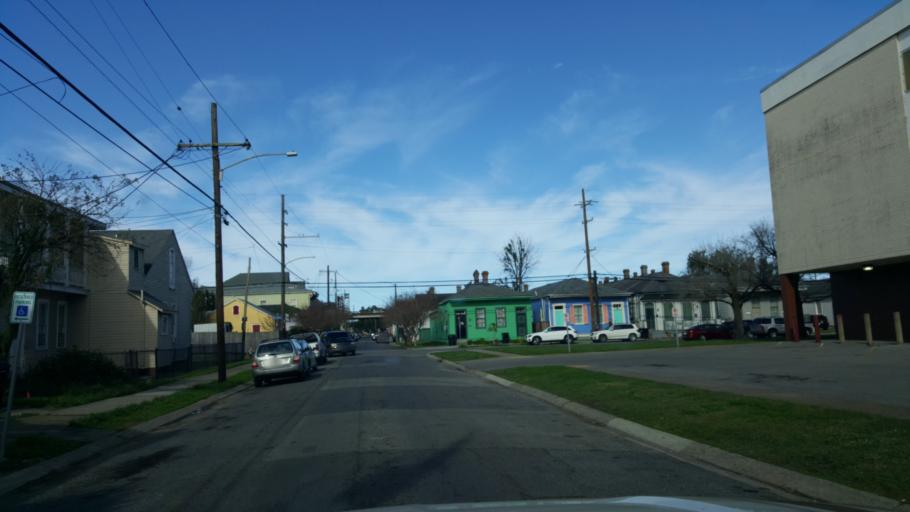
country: US
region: Louisiana
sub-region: Orleans Parish
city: New Orleans
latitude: 29.9687
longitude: -90.0657
